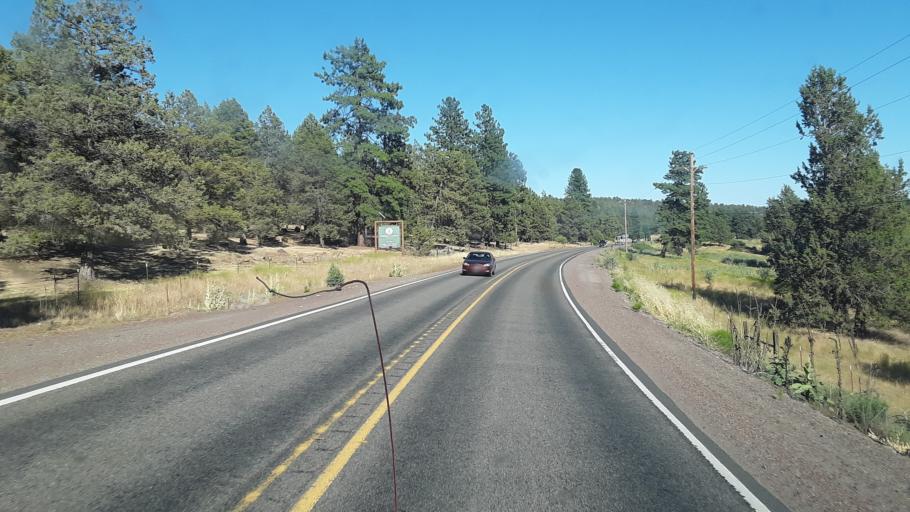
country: US
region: Oregon
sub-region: Klamath County
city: Klamath Falls
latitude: 42.2746
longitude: -121.8909
